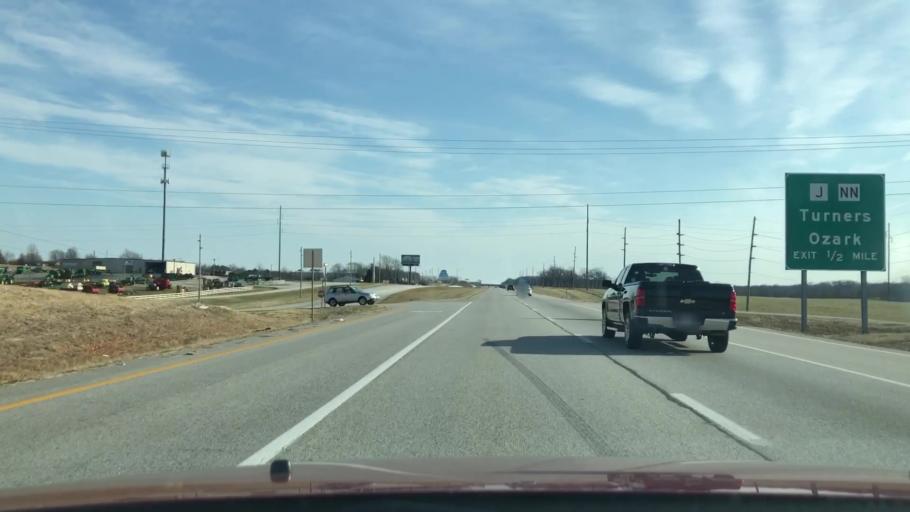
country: US
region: Missouri
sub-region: Christian County
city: Ozark
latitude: 37.1205
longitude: -93.2005
